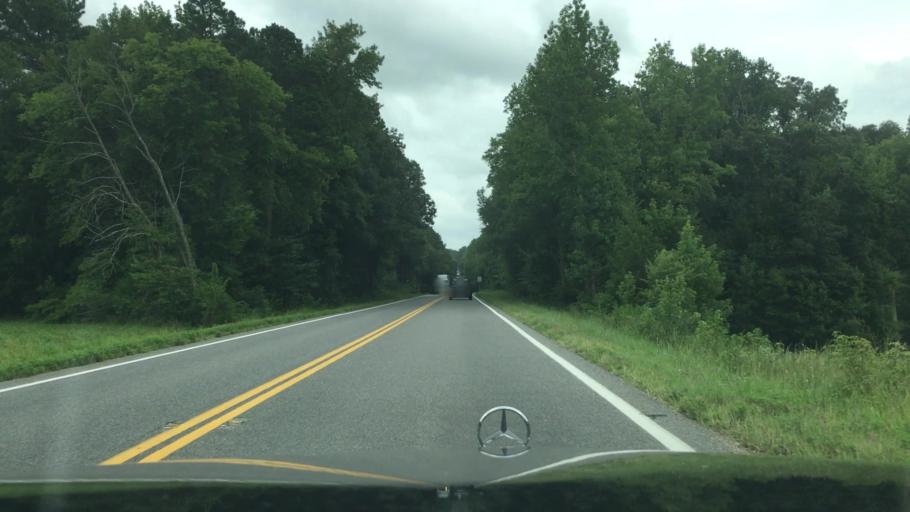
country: US
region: Virginia
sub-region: Nottoway County
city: Crewe
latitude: 37.2772
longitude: -78.1819
